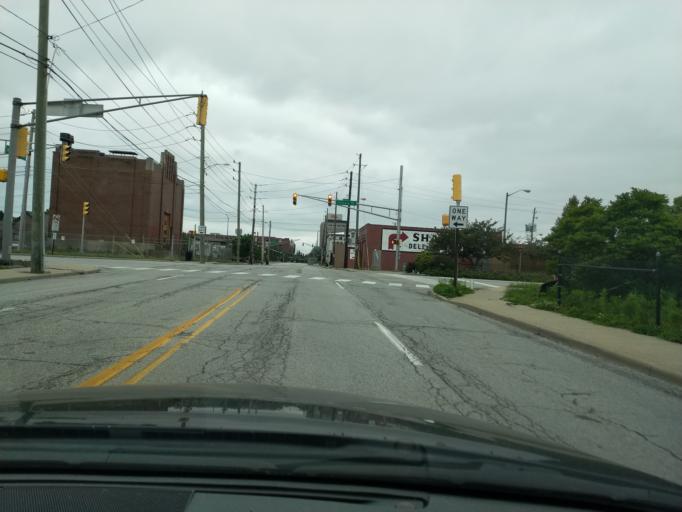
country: US
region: Indiana
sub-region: Marion County
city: Indianapolis
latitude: 39.7565
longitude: -86.1609
